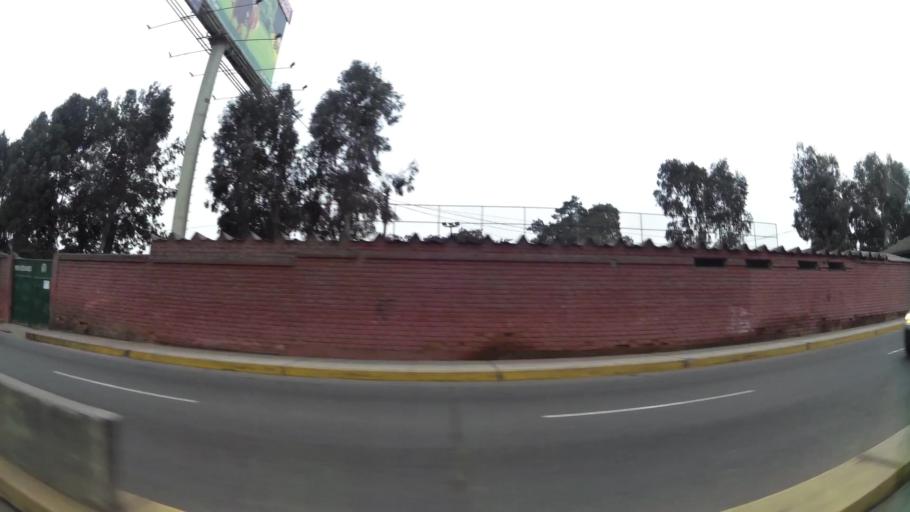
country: PE
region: Lima
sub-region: Lima
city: San Luis
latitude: -12.0985
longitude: -76.9773
